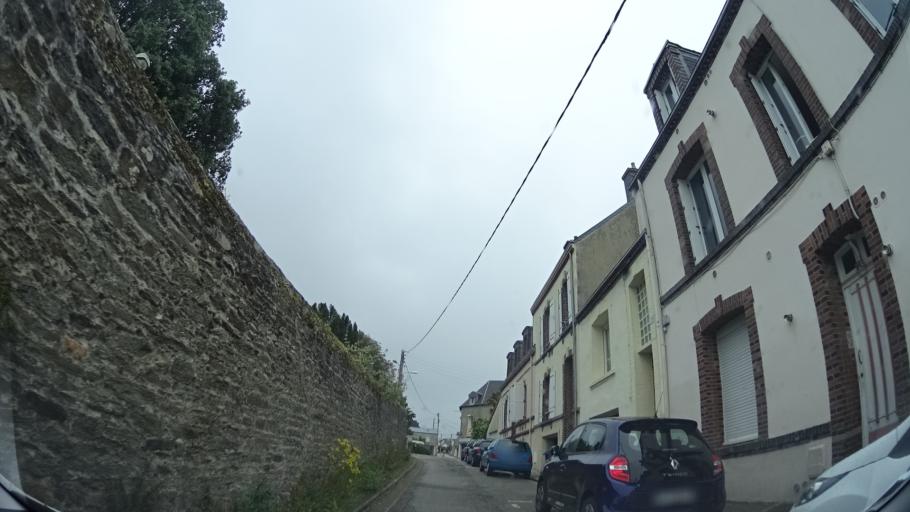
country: FR
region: Lower Normandy
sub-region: Departement de la Manche
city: Octeville
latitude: 49.6317
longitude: -1.6324
